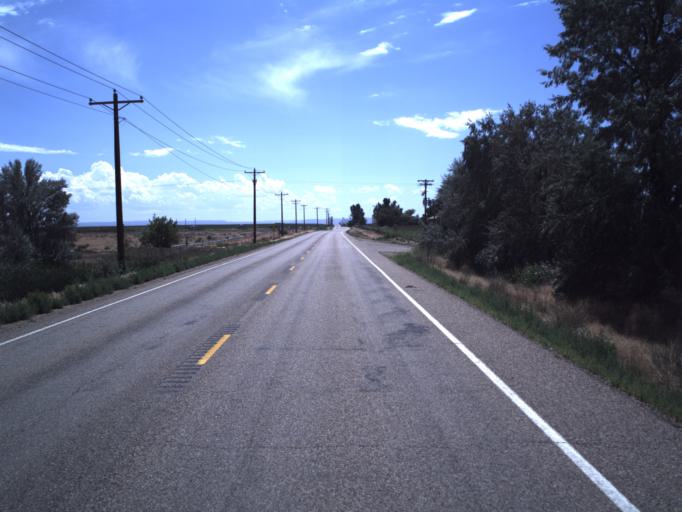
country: US
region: Utah
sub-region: Uintah County
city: Naples
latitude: 40.1864
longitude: -109.6646
